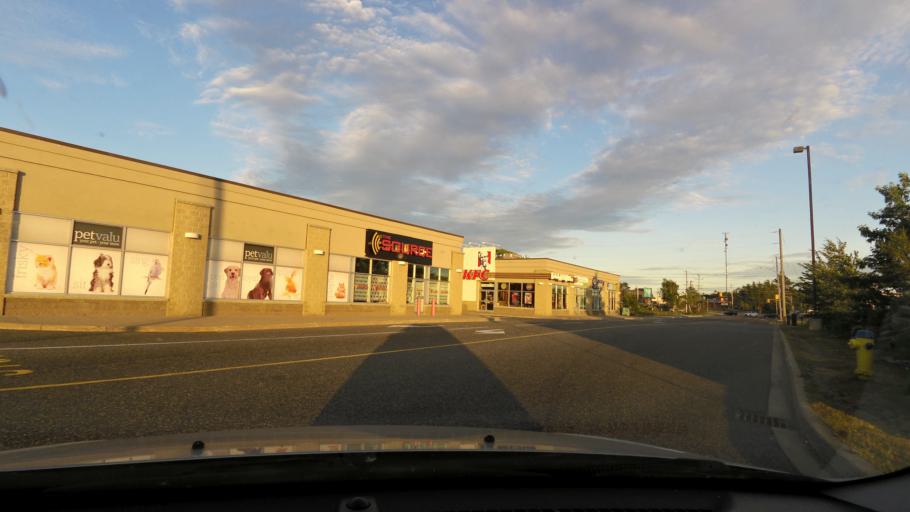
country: CA
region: Ontario
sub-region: Parry Sound District
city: Parry Sound
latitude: 45.3456
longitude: -80.0111
